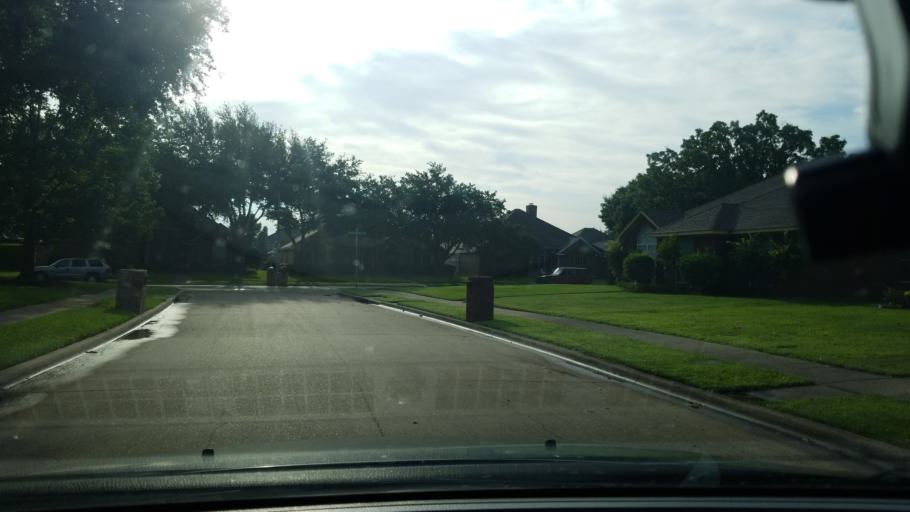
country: US
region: Texas
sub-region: Dallas County
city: Mesquite
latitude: 32.7958
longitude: -96.6057
